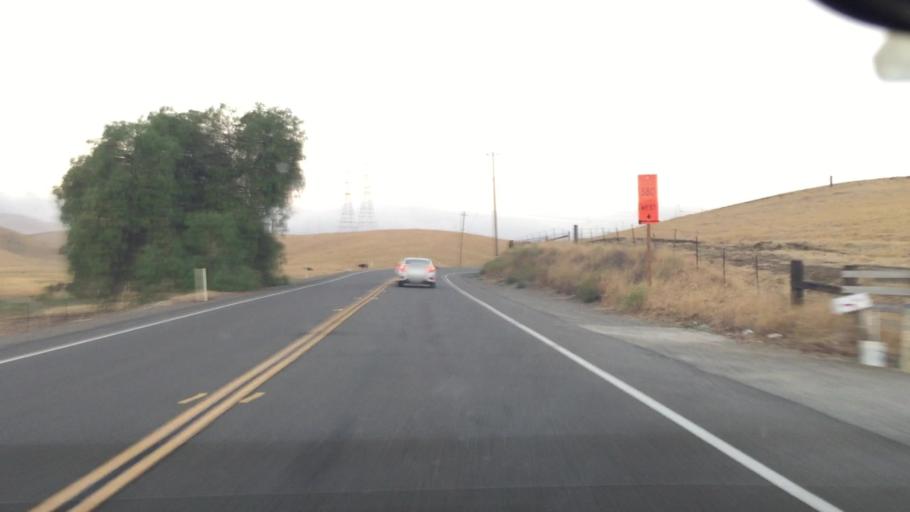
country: US
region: California
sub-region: San Joaquin County
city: Mountain House
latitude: 37.7444
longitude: -121.5912
